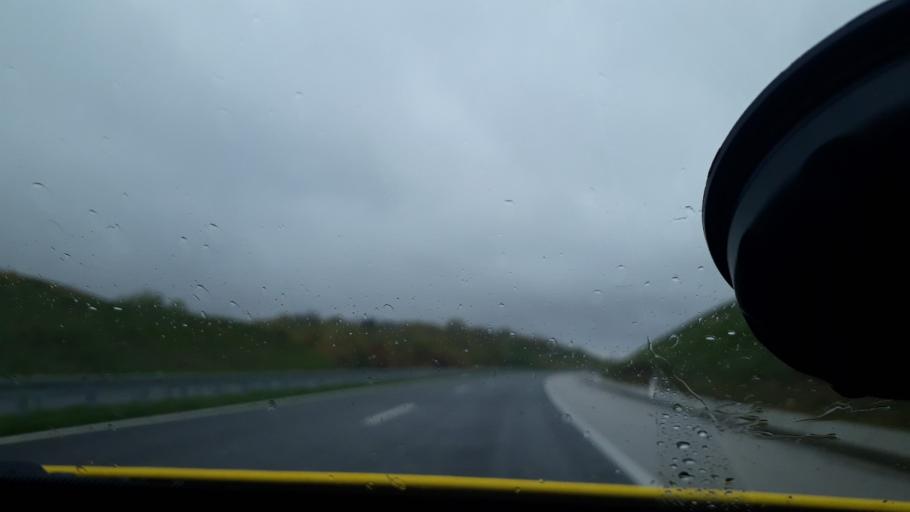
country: BA
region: Republika Srpska
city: Derventa
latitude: 44.8416
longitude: 17.9548
